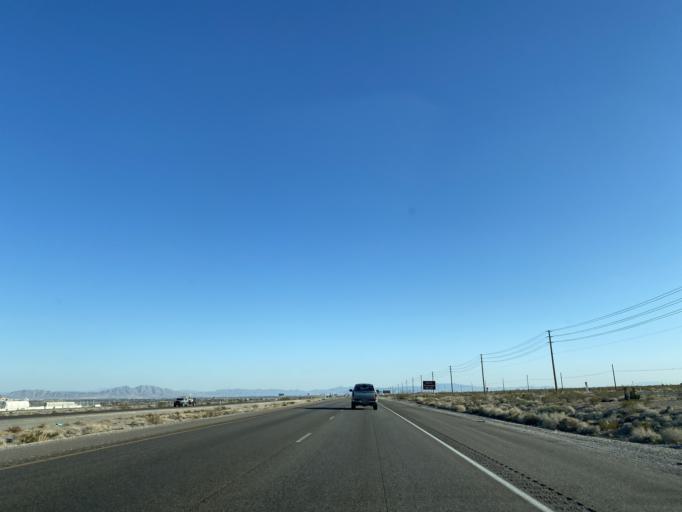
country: US
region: Nevada
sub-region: Clark County
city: Summerlin South
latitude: 36.3356
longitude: -115.3200
